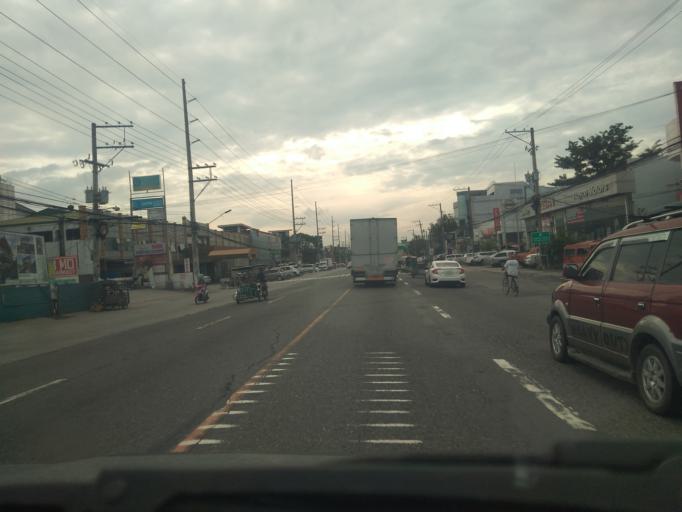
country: PH
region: Central Luzon
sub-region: Province of Pampanga
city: Magliman
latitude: 15.0438
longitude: 120.6741
